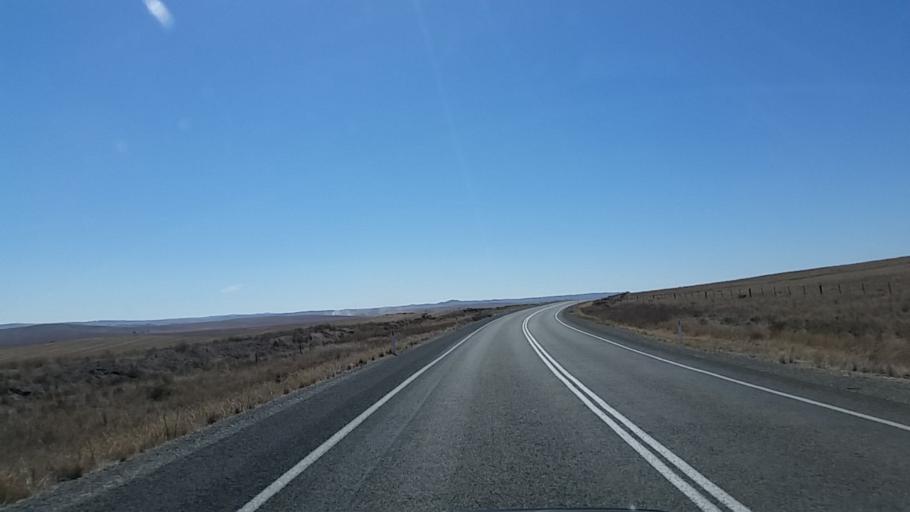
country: AU
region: South Australia
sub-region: Northern Areas
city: Jamestown
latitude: -33.3236
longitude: 138.8845
